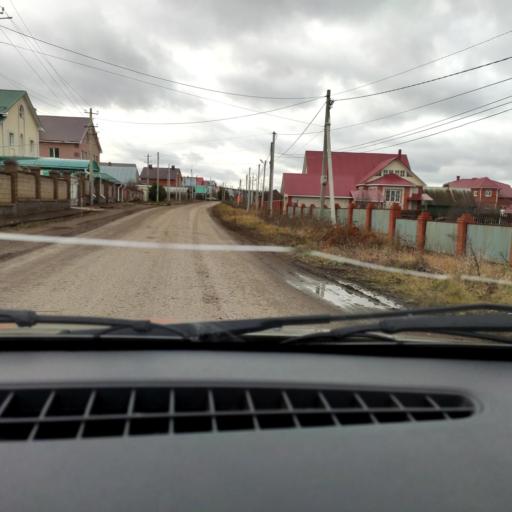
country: RU
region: Bashkortostan
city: Avdon
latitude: 54.4904
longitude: 55.8598
